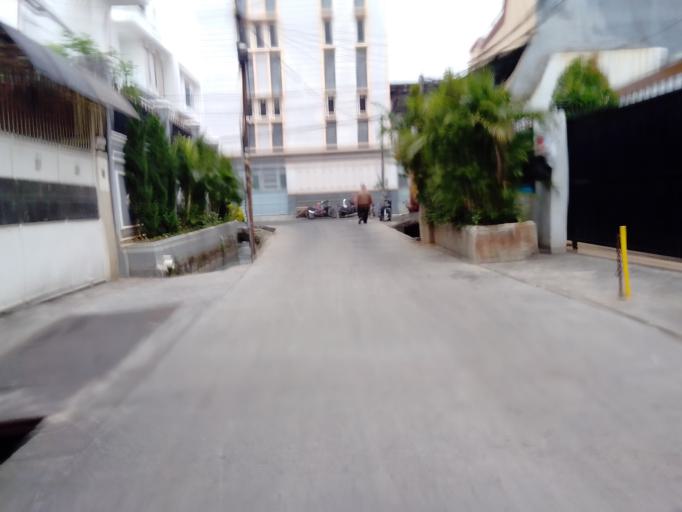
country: ID
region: Jakarta Raya
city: Jakarta
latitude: -6.1573
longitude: 106.8155
